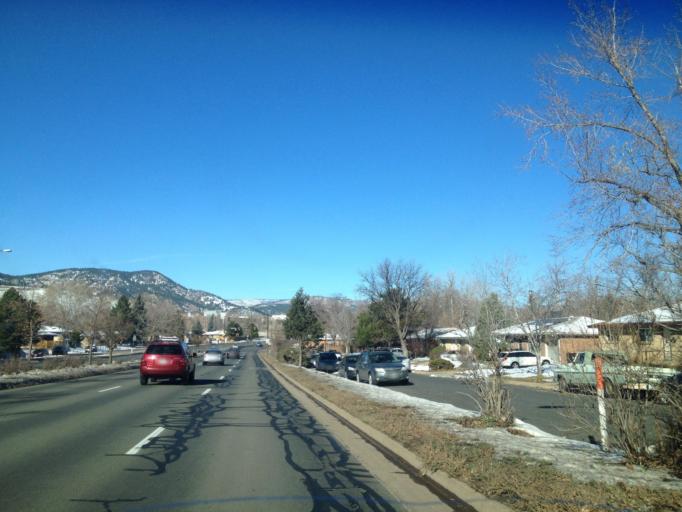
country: US
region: Colorado
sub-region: Boulder County
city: Boulder
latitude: 39.9879
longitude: -105.2528
